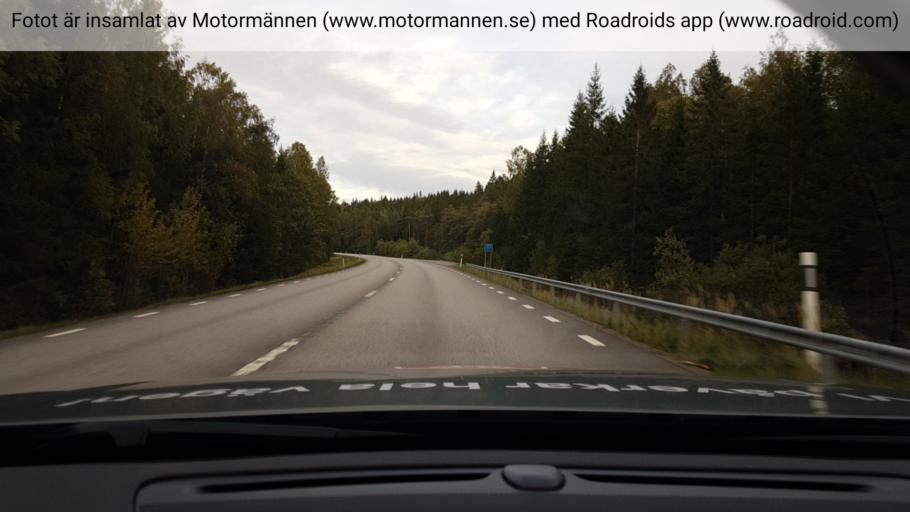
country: SE
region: Vaestra Goetaland
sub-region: Bengtsfors Kommun
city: Dals Langed
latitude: 59.0285
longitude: 12.4116
